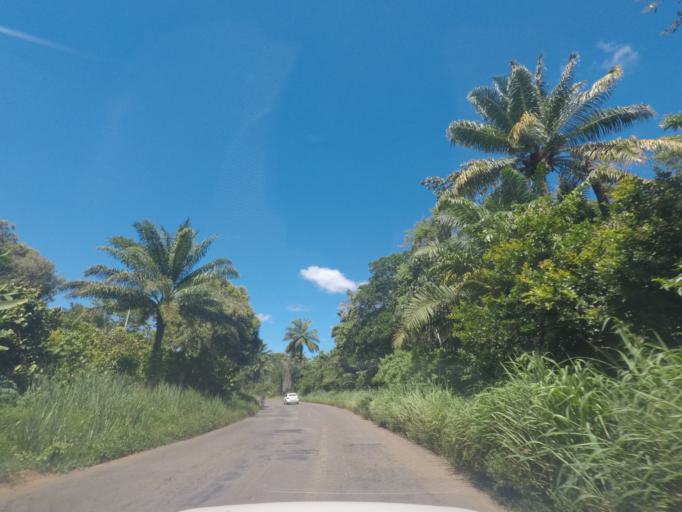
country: BR
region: Bahia
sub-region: Taperoa
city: Taperoa
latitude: -13.4942
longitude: -39.0939
